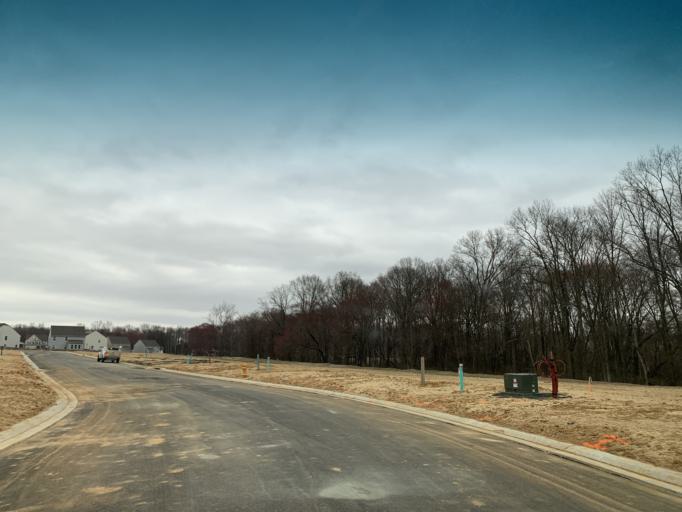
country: US
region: Maryland
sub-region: Harford County
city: Aberdeen
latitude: 39.5390
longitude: -76.1940
